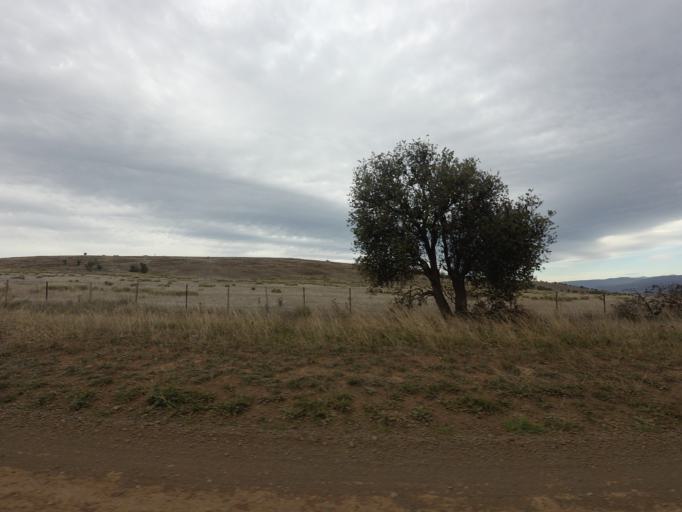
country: AU
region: Tasmania
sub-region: Derwent Valley
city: New Norfolk
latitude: -42.5526
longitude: 146.8974
